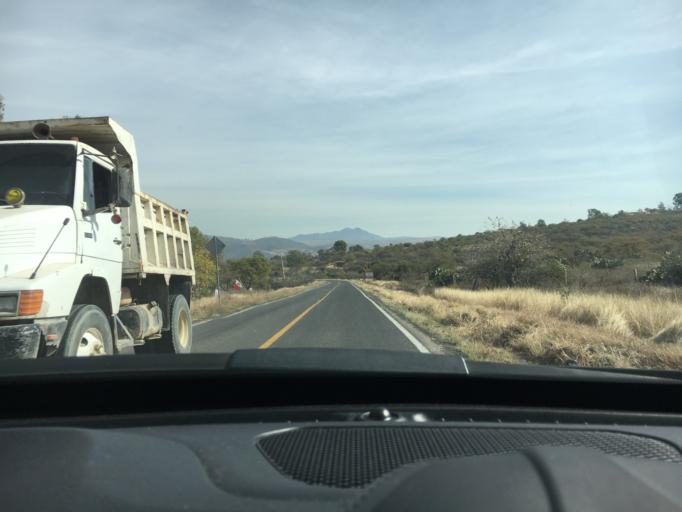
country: MX
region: Guanajuato
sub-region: Silao de la Victoria
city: San Francisco (Banos de Agua Caliente)
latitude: 21.0669
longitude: -101.4990
